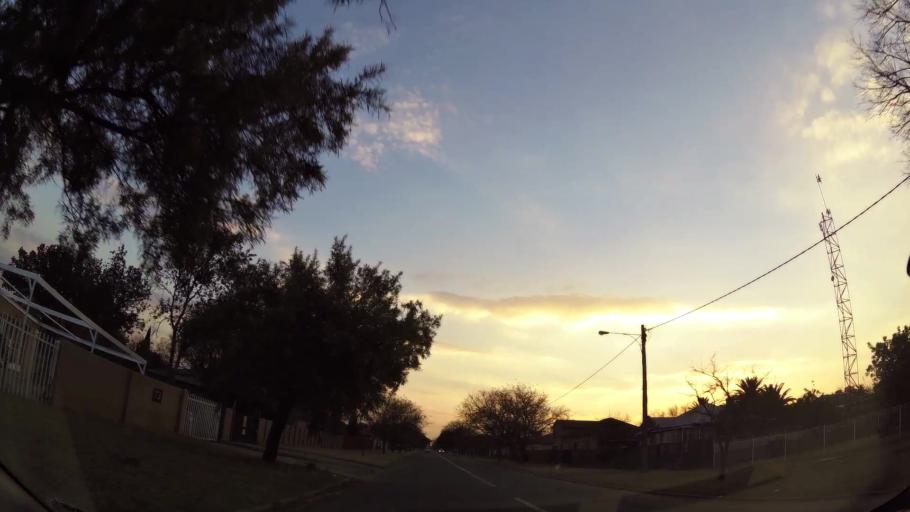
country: ZA
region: Gauteng
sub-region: Ekurhuleni Metropolitan Municipality
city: Benoni
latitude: -26.1776
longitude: 28.3170
